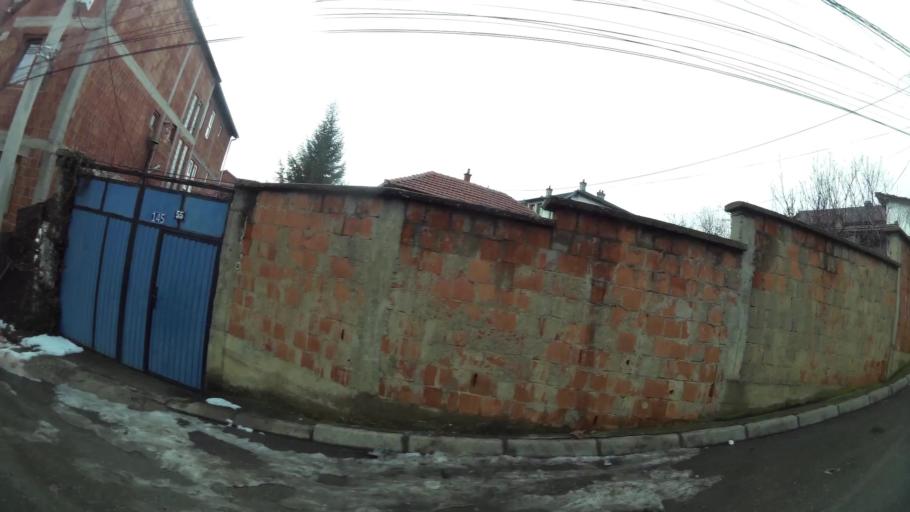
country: XK
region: Pristina
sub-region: Komuna e Prishtines
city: Pristina
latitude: 42.6740
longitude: 21.1590
